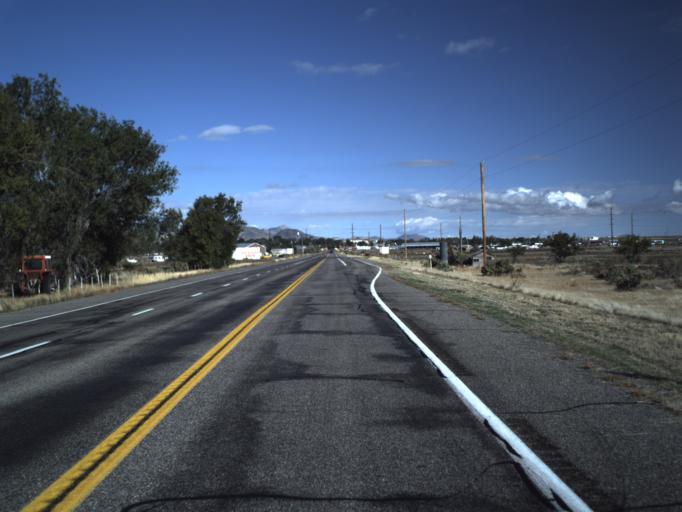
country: US
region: Utah
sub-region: Beaver County
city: Milford
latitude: 38.3771
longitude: -113.0012
